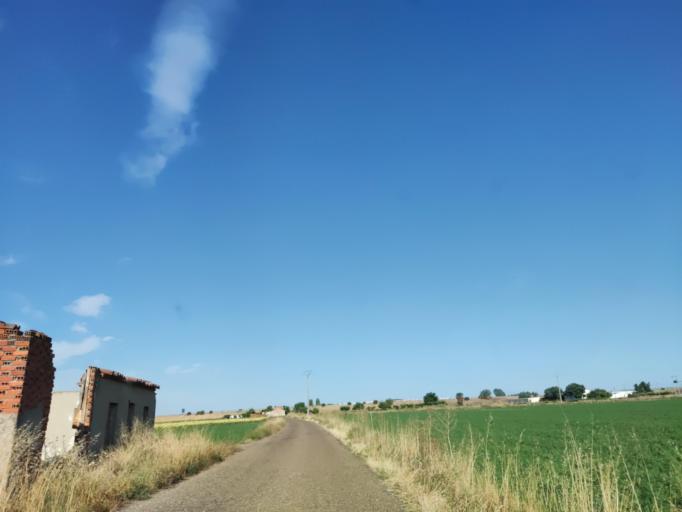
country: ES
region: Castille and Leon
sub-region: Provincia de Zamora
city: Zamora
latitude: 41.4992
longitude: -5.7236
